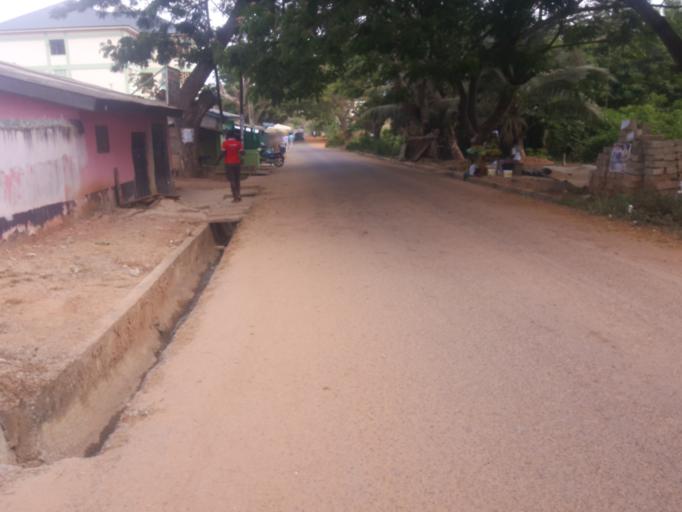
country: GH
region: Central
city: Cape Coast
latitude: 5.1111
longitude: -1.2917
